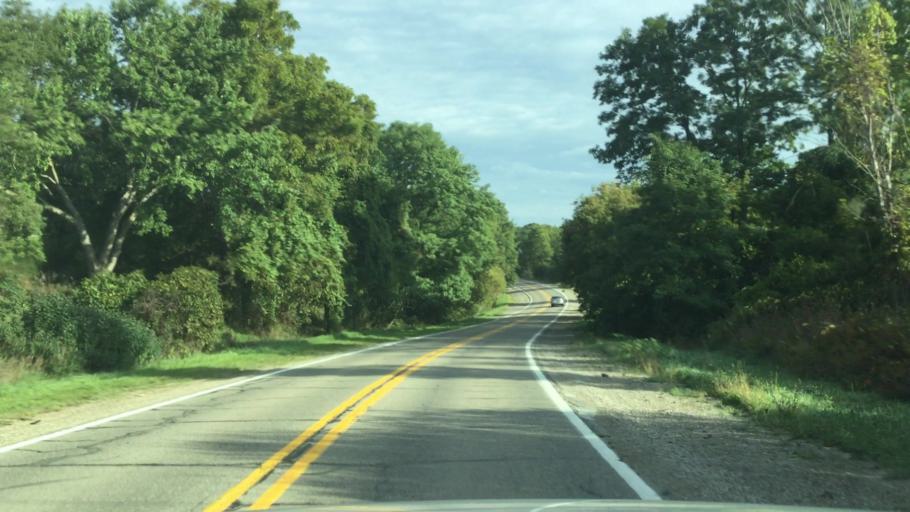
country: US
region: Michigan
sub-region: Livingston County
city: Brighton
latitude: 42.4970
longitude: -83.8596
